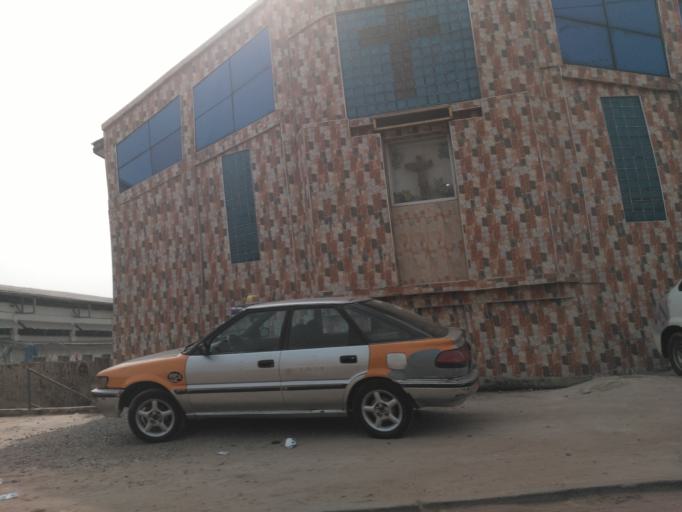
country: GH
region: Ashanti
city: Kumasi
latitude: 6.6841
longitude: -1.6135
